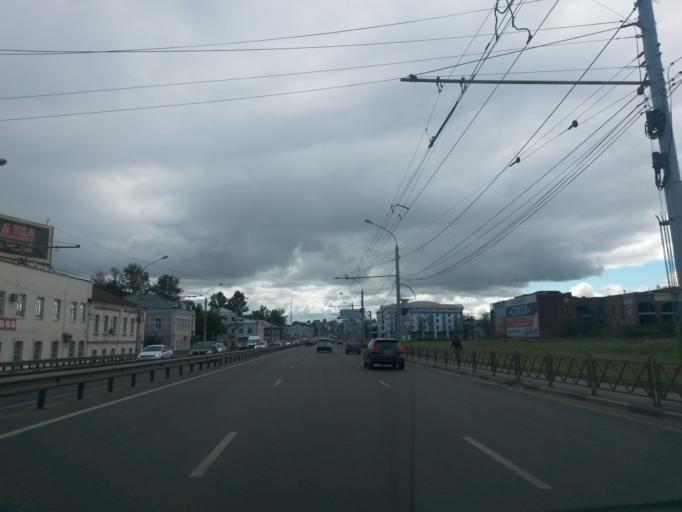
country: RU
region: Jaroslavl
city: Yaroslavl
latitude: 57.6146
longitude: 39.8837
